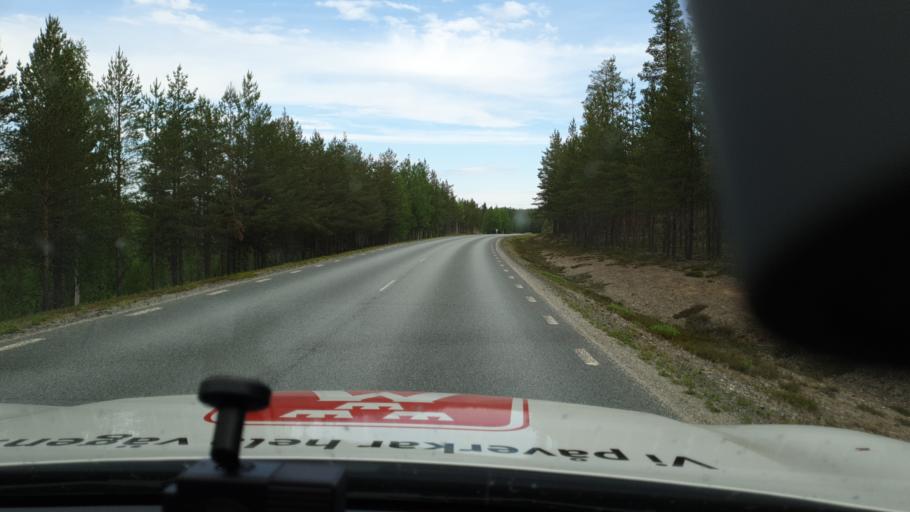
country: SE
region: Vaesterbotten
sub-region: Mala Kommun
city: Mala
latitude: 65.0572
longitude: 18.3829
